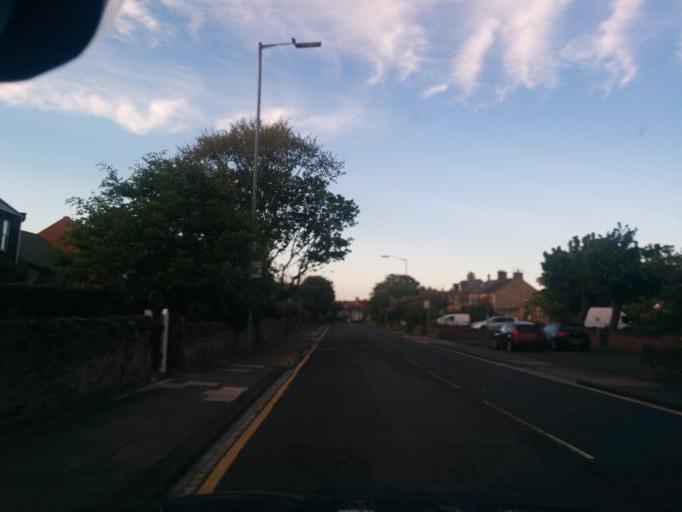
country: GB
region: England
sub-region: Northumberland
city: Newbiggin-by-the-Sea
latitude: 55.1835
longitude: -1.5154
